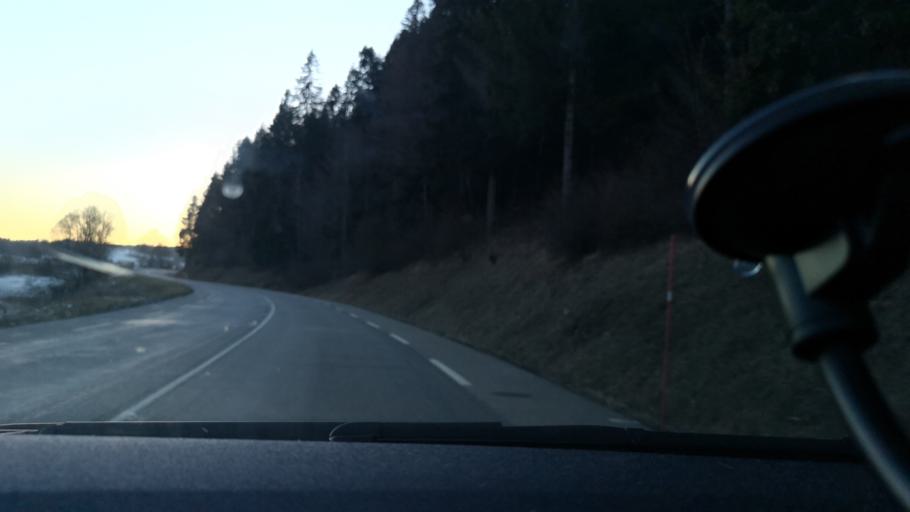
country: FR
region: Franche-Comte
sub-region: Departement du Doubs
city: La Cluse-et-Mijoux
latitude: 46.8658
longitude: 6.3565
